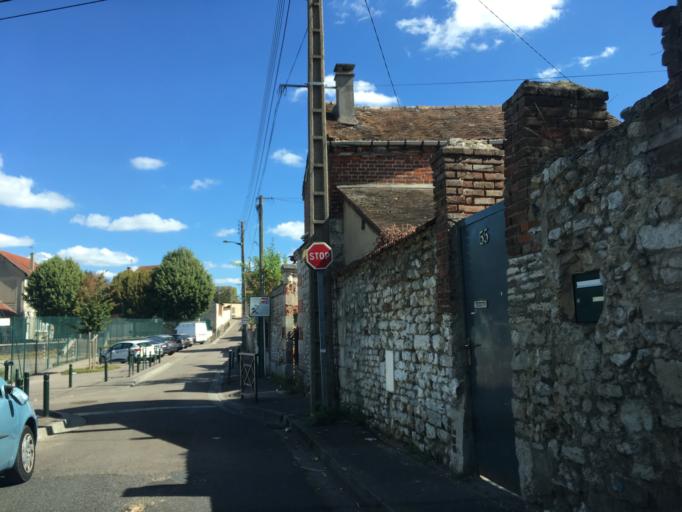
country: FR
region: Haute-Normandie
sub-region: Departement de l'Eure
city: Vernon
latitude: 49.0848
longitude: 1.4938
